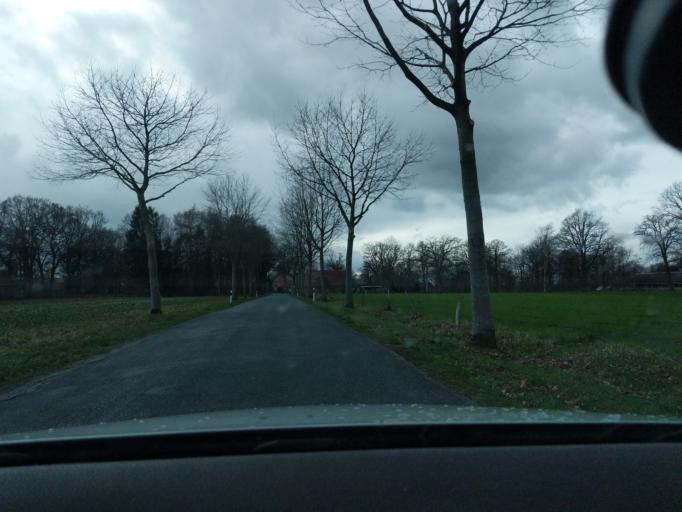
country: DE
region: Lower Saxony
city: Kranenburg
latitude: 53.5986
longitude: 9.1903
